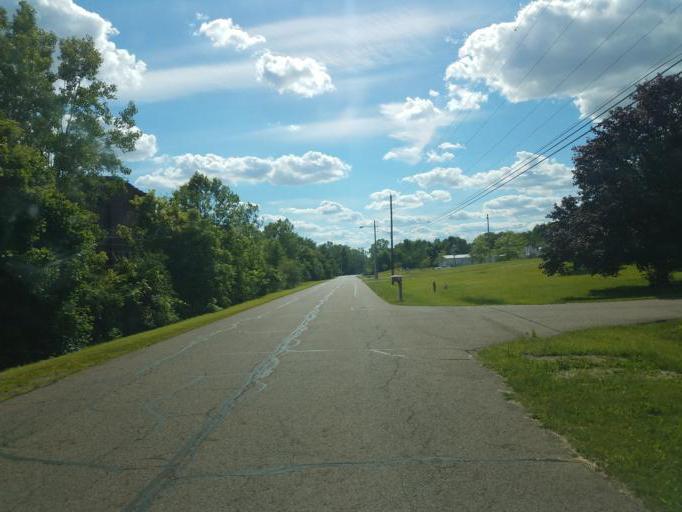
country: US
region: Ohio
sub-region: Morrow County
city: Mount Gilead
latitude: 40.5511
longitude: -82.8398
